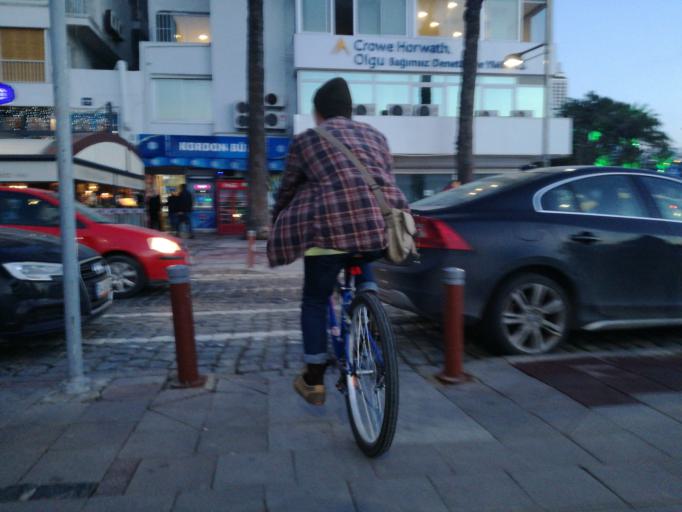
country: TR
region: Izmir
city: Izmir
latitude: 38.4300
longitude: 27.1342
